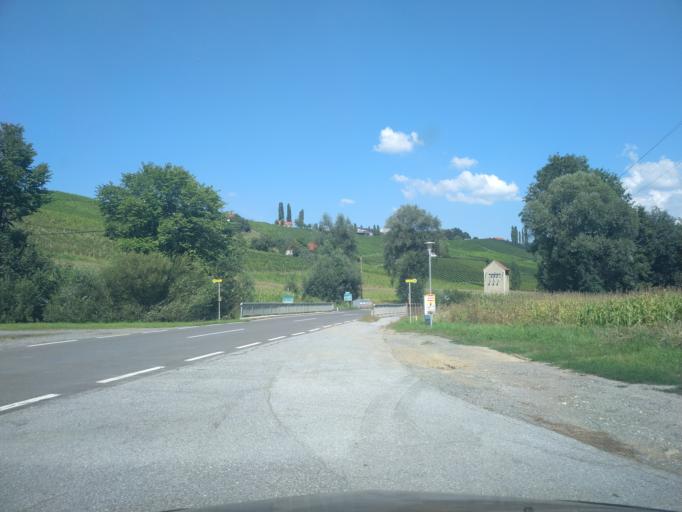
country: AT
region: Styria
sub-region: Politischer Bezirk Leibnitz
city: Gamlitz
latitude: 46.7165
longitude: 15.5141
